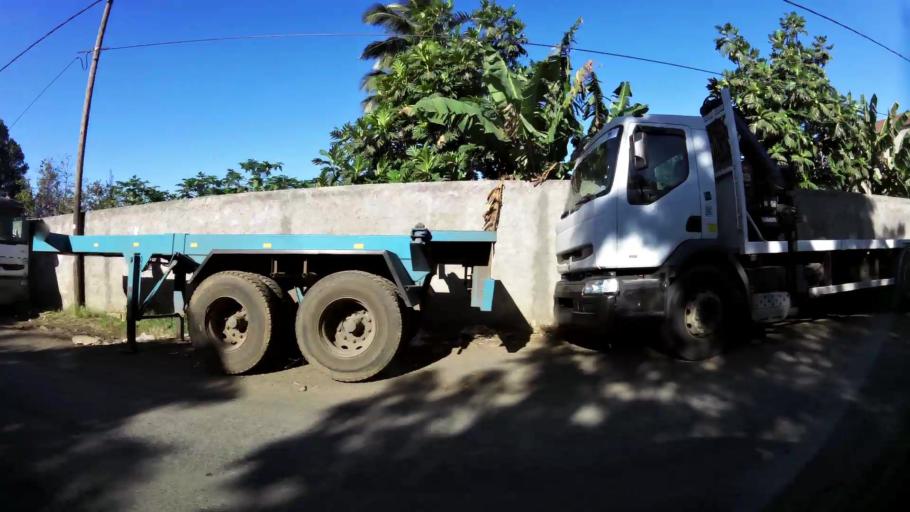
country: YT
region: Mamoudzou
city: Mamoudzou
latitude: -12.7645
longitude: 45.2272
